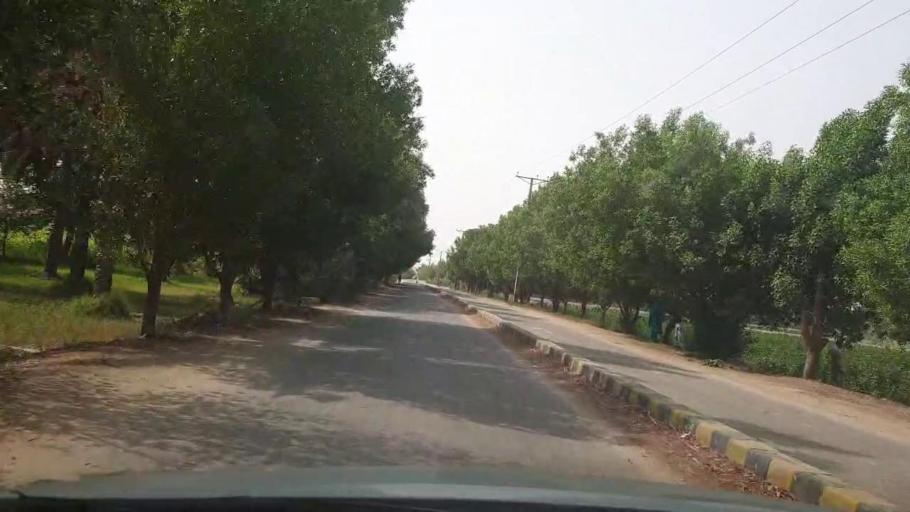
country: PK
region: Sindh
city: Kot Diji
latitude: 27.3517
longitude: 68.7118
